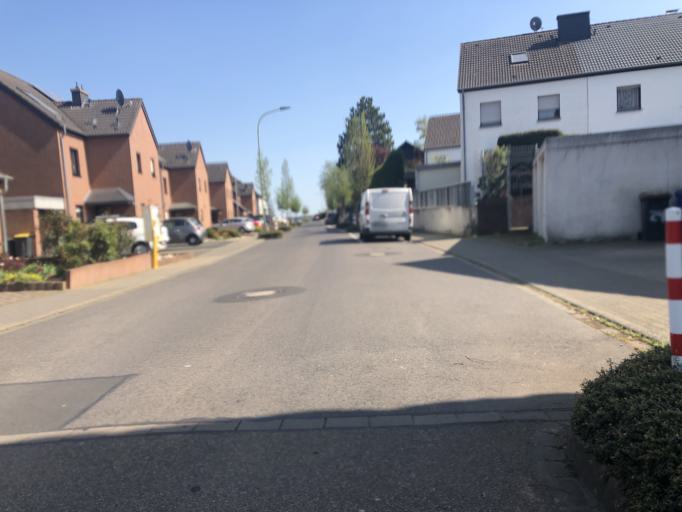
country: DE
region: North Rhine-Westphalia
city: Zulpich
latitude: 50.6941
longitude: 6.6578
